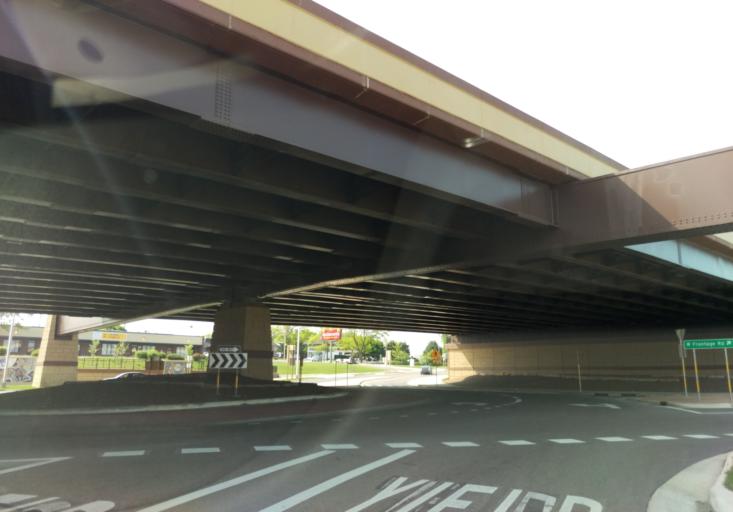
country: US
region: Wisconsin
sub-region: Dane County
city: Shorewood Hills
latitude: 43.0337
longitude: -89.4576
